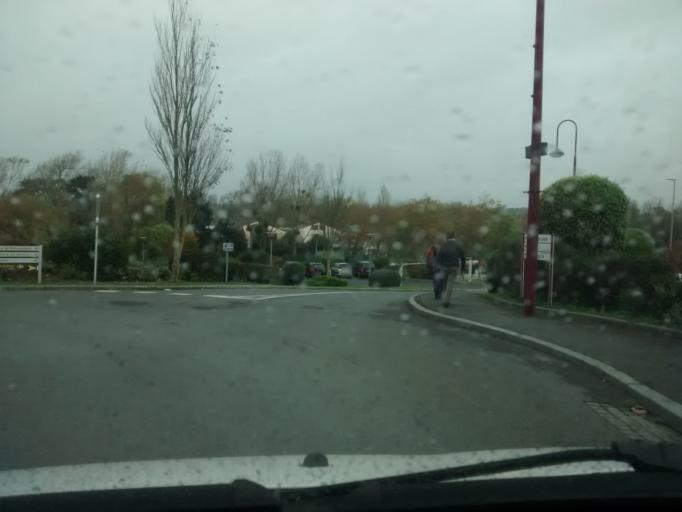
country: FR
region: Lower Normandy
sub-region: Departement de la Manche
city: Saint-Pair-sur-Mer
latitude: 48.8162
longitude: -1.5705
